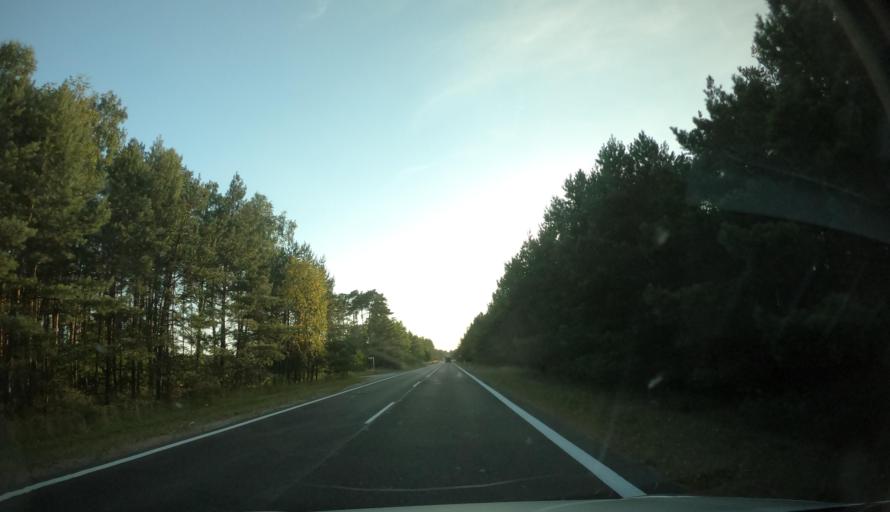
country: PL
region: Kujawsko-Pomorskie
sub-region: Powiat bydgoski
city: Koronowo
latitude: 53.3115
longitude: 17.9990
